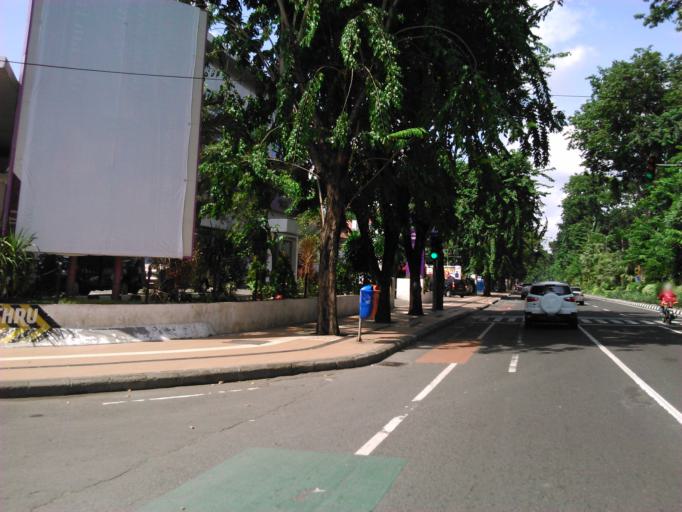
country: ID
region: East Java
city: Gubengairlangga
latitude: -7.2870
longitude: 112.7397
